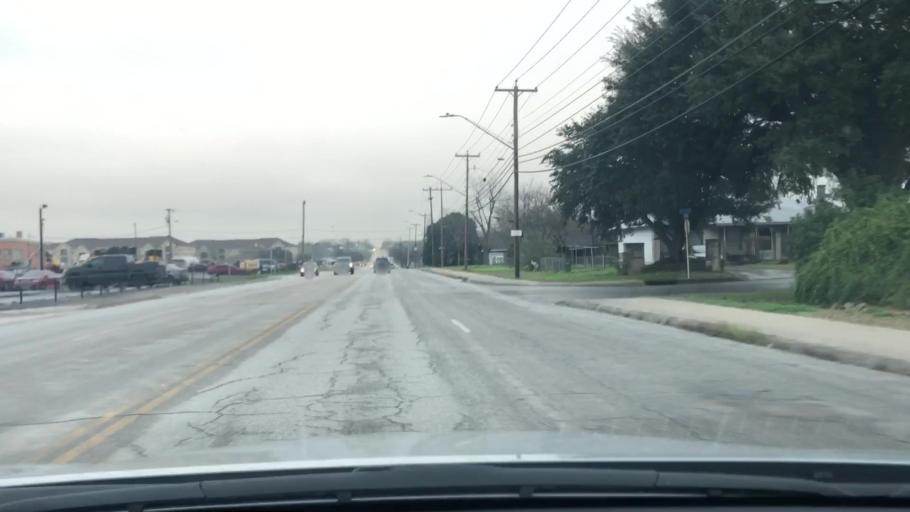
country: US
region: Texas
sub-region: Bexar County
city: Terrell Hills
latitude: 29.4355
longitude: -98.4277
